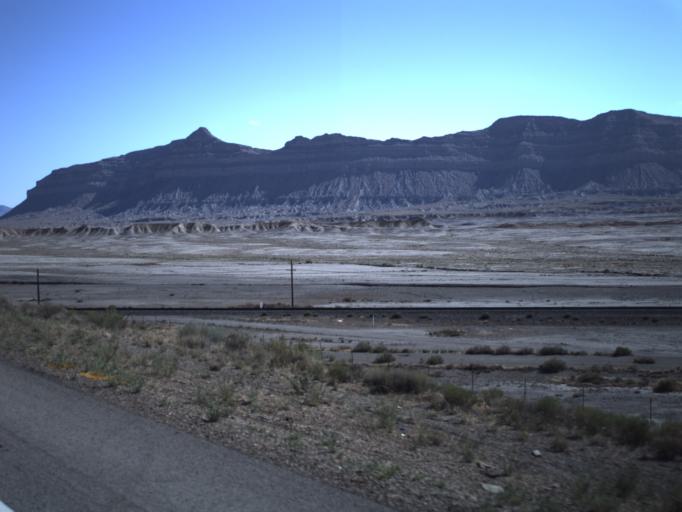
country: US
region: Utah
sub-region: Carbon County
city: East Carbon City
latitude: 39.1341
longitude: -110.3377
